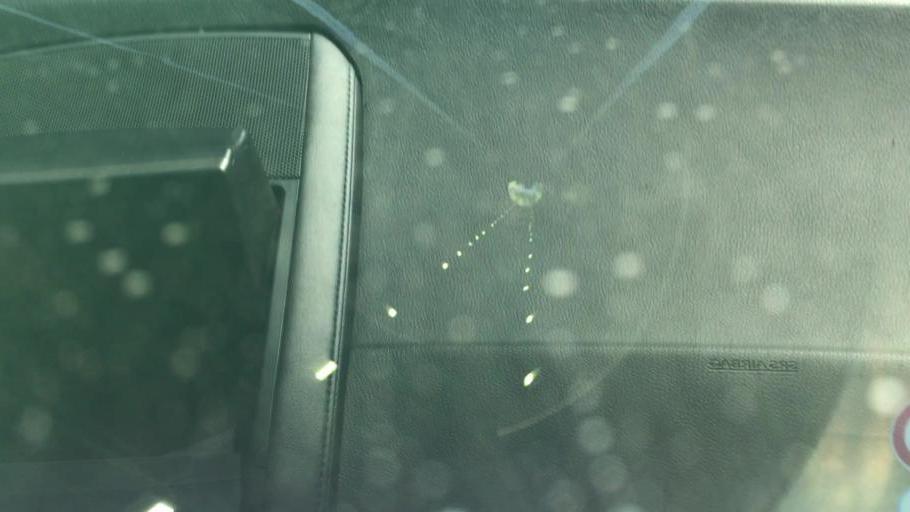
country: JP
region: Hokkaido
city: Shimo-furano
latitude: 42.9633
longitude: 142.6449
